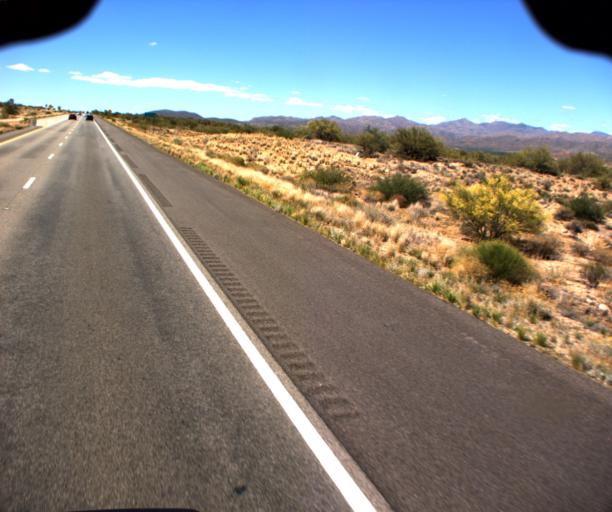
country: US
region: Arizona
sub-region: Mohave County
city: Kingman
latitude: 34.8660
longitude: -113.6429
